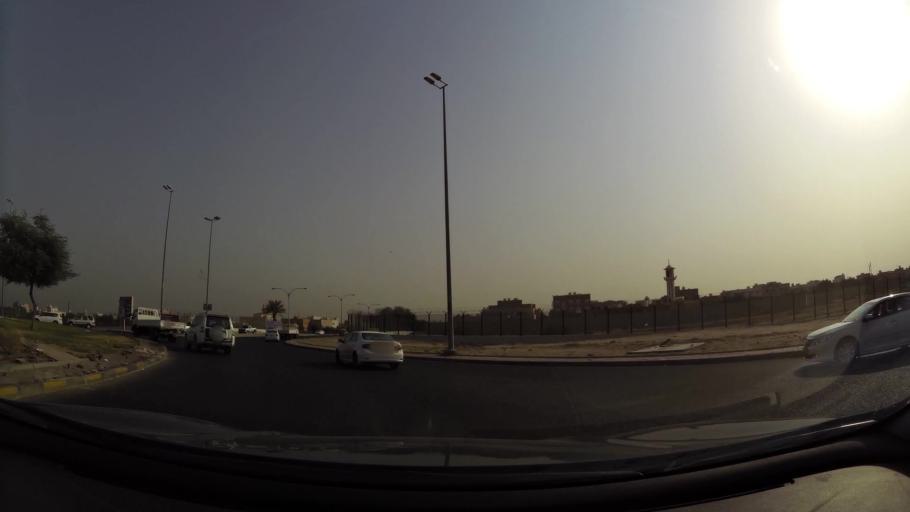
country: KW
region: Al Ahmadi
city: Ar Riqqah
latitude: 29.1213
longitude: 48.1045
